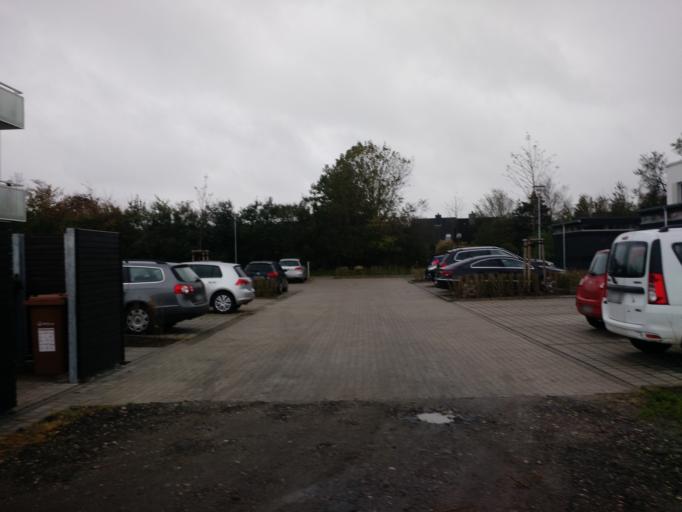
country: DE
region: Schleswig-Holstein
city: Husum
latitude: 54.4923
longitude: 9.0313
